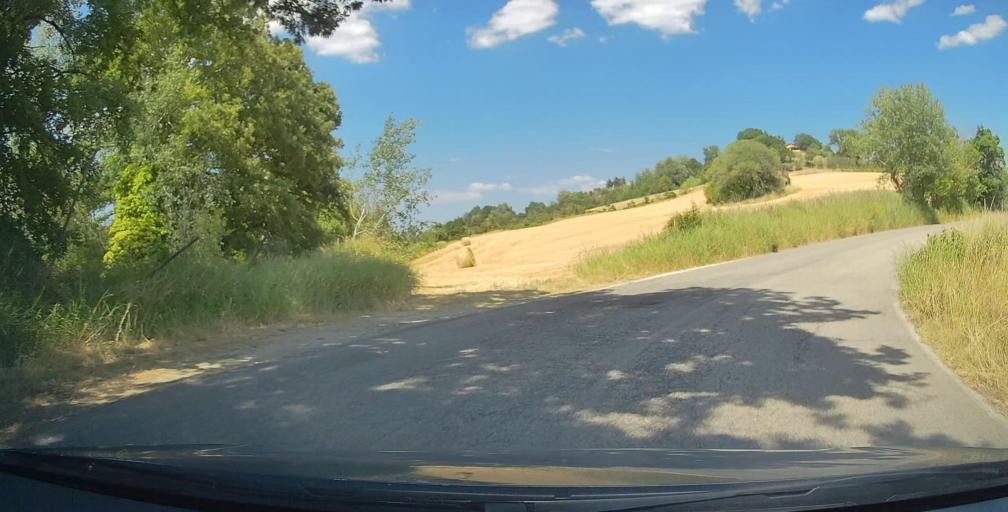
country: IT
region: Umbria
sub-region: Provincia di Terni
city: Otricoli
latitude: 42.3999
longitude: 12.4878
